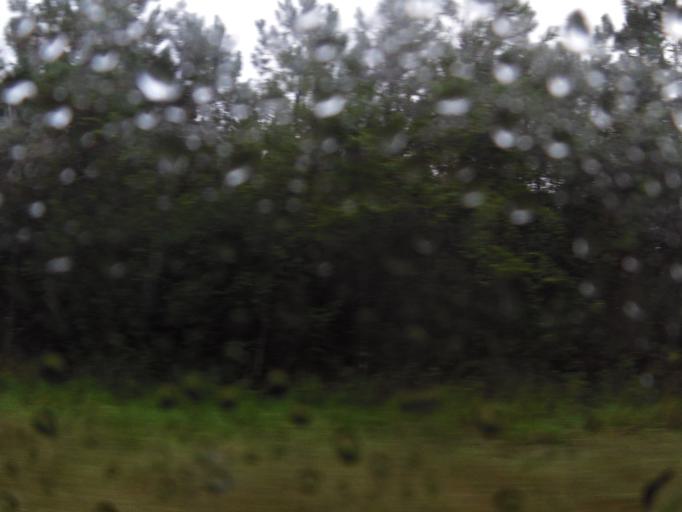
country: US
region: Florida
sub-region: Nassau County
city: Hilliard
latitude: 30.5404
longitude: -82.0399
